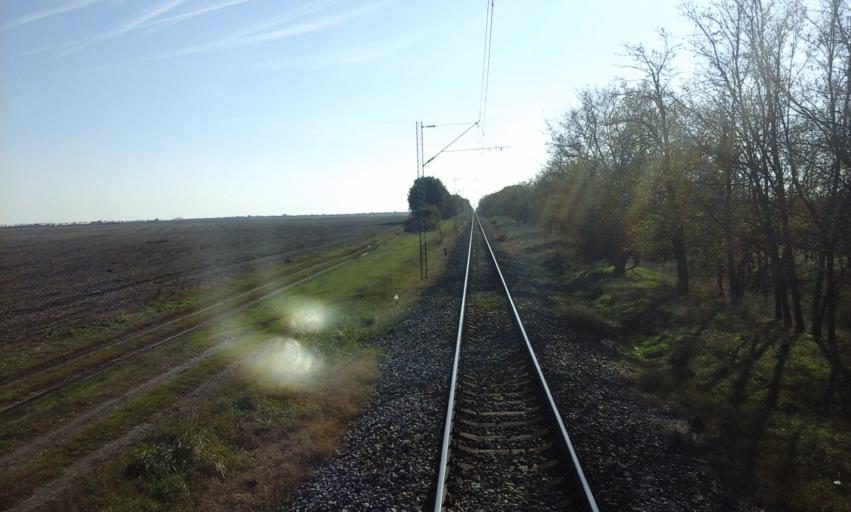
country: RS
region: Autonomna Pokrajina Vojvodina
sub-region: Severnobacki Okrug
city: Backa Topola
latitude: 45.8723
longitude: 19.6579
